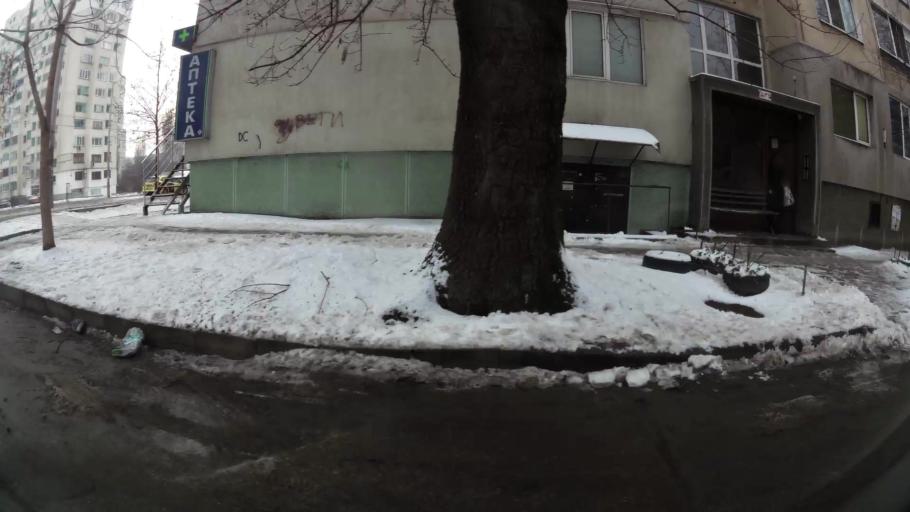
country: BG
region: Sofia-Capital
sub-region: Stolichna Obshtina
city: Sofia
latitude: 42.7107
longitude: 23.3001
